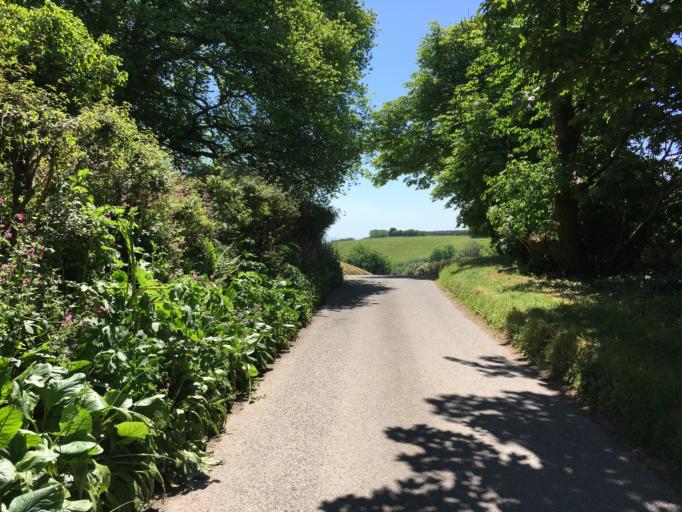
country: GB
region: England
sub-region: Devon
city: Dartmouth
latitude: 50.3492
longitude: -3.5371
